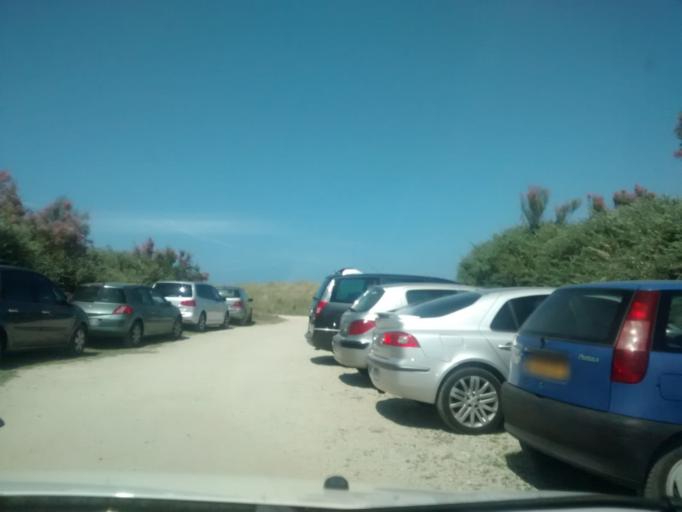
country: FR
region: Brittany
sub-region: Departement d'Ille-et-Vilaine
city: Cancale
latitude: 48.6949
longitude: -1.8783
